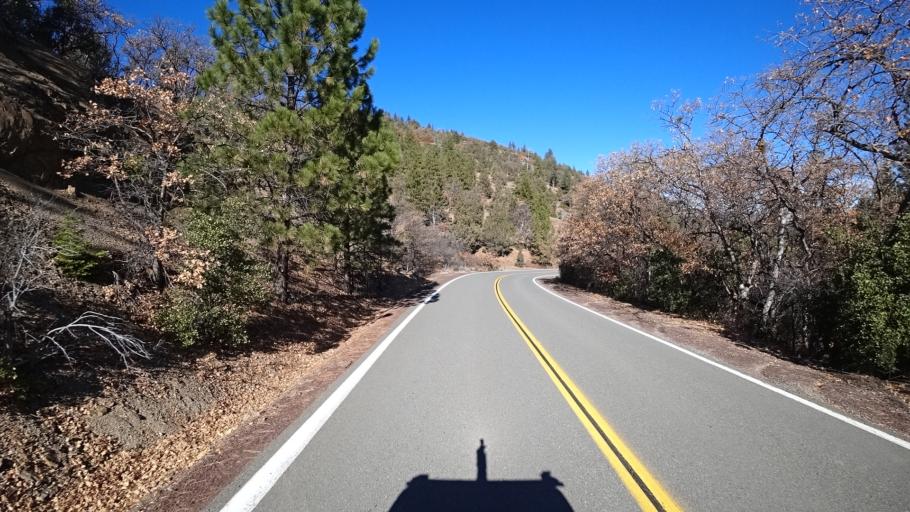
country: US
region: California
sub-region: Siskiyou County
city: Weed
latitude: 41.4493
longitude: -122.6411
